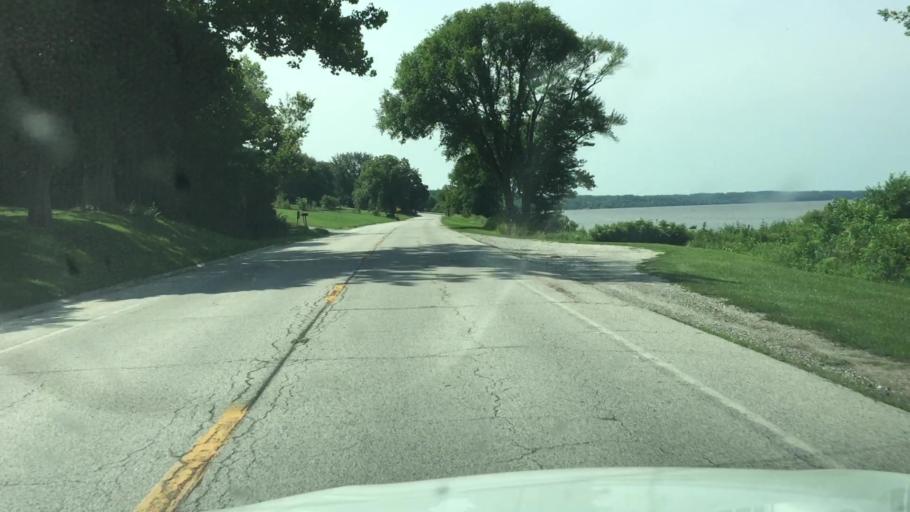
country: US
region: Illinois
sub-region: Hancock County
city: Nauvoo
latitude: 40.5249
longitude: -91.3677
